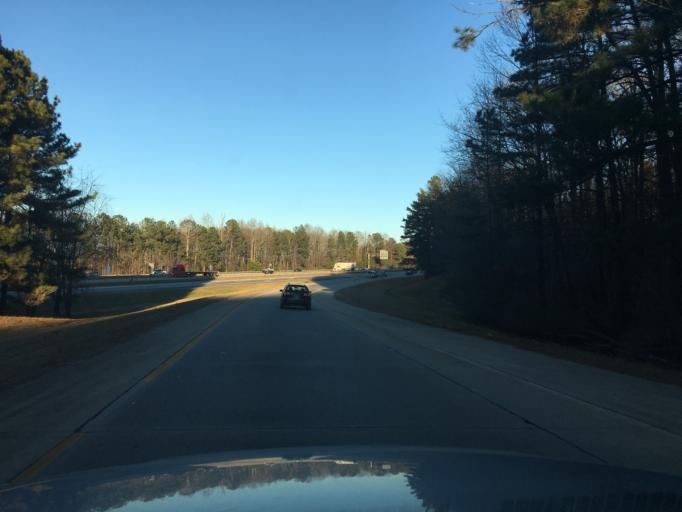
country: US
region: Georgia
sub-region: Carroll County
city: Villa Rica
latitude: 33.7215
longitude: -84.9366
